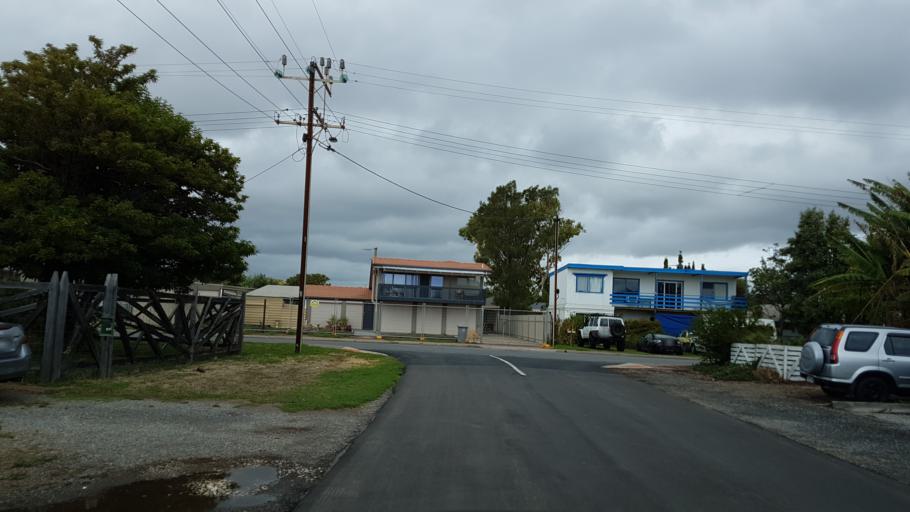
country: AU
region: South Australia
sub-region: Onkaparinga
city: Port Willunga
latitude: -35.2763
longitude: 138.4451
